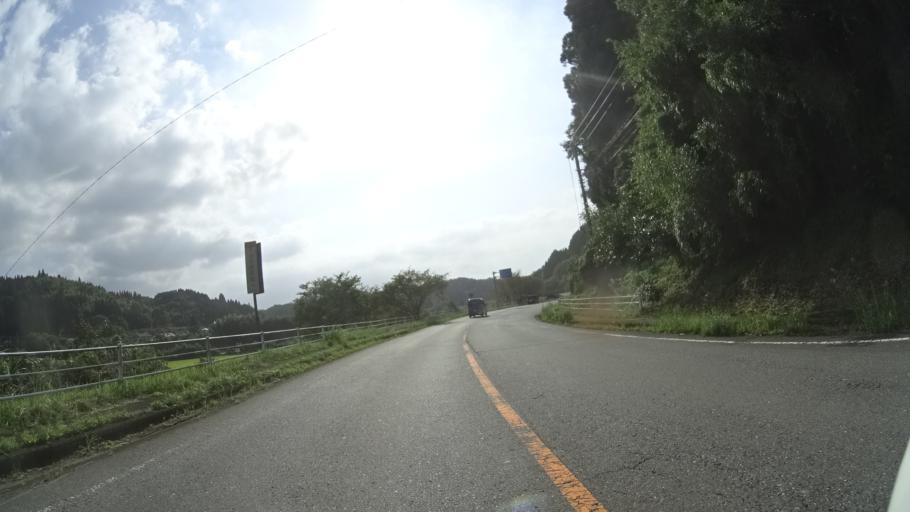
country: JP
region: Kumamoto
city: Aso
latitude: 32.6878
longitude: 131.0841
